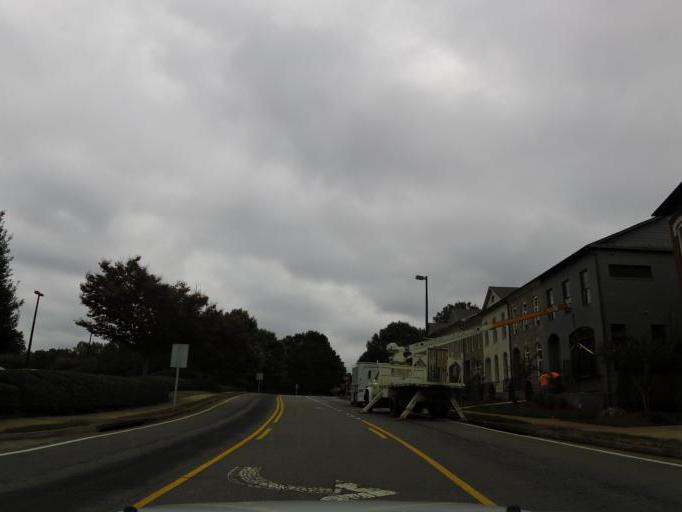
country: US
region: Georgia
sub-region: Cobb County
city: Kennesaw
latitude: 34.0386
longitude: -84.5678
